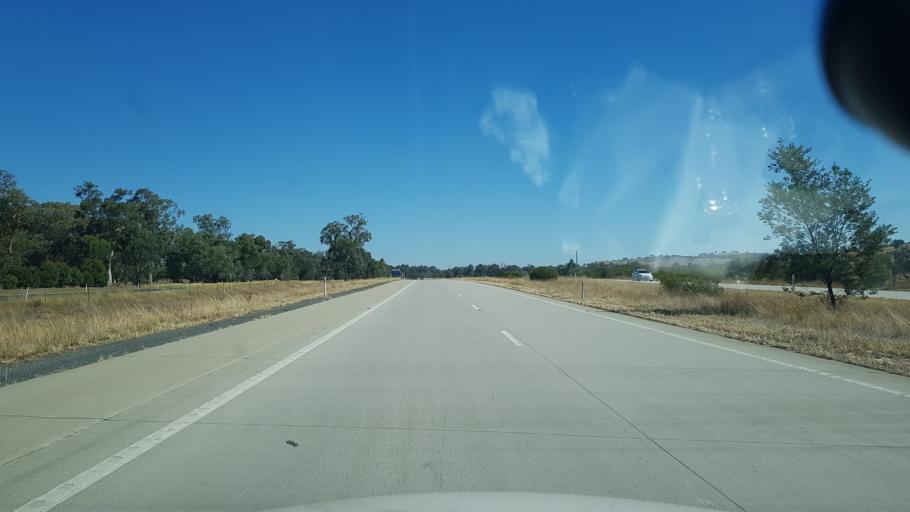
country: AU
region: New South Wales
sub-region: Greater Hume Shire
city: Holbrook
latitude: -35.9076
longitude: 147.1589
